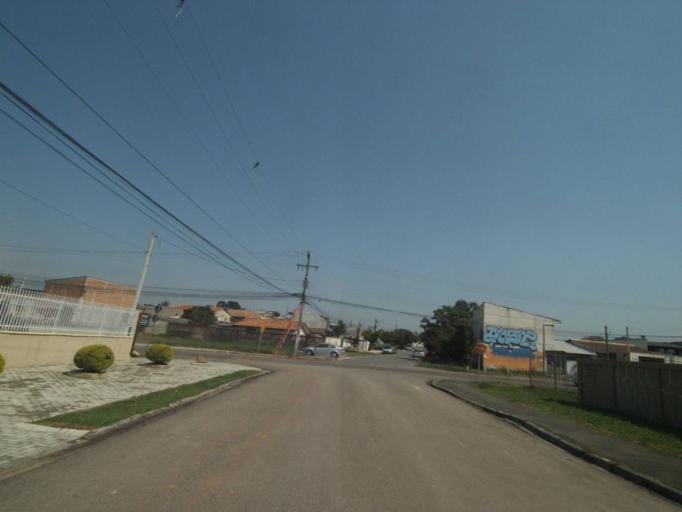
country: BR
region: Parana
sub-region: Sao Jose Dos Pinhais
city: Sao Jose dos Pinhais
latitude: -25.5214
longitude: -49.2700
